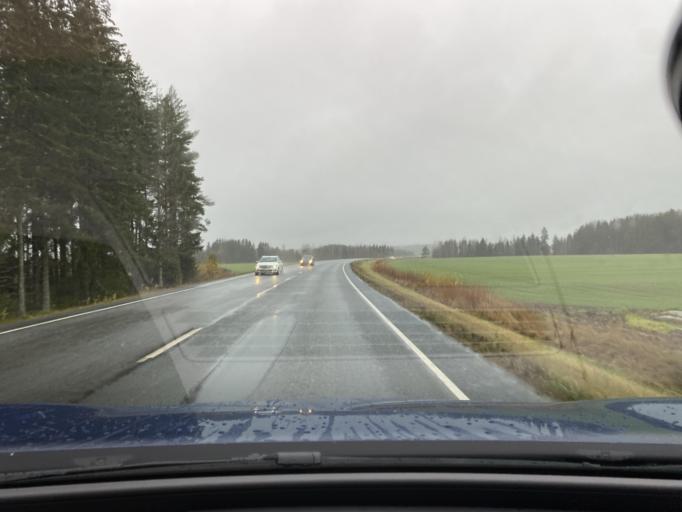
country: FI
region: Varsinais-Suomi
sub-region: Loimaa
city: Loimaa
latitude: 60.8812
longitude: 22.9828
